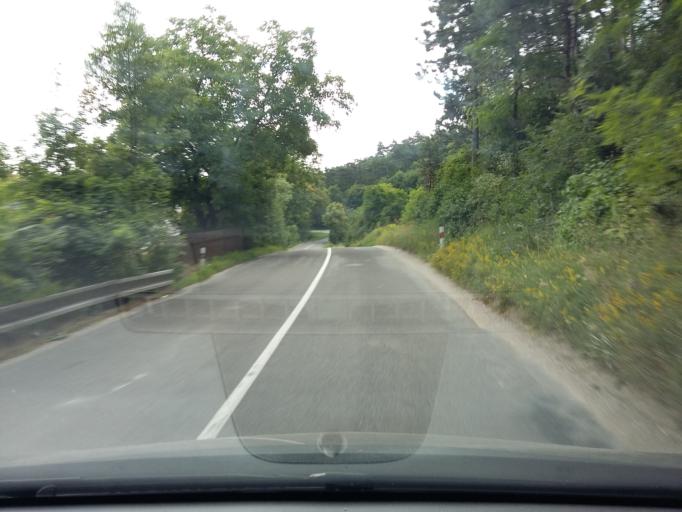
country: SK
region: Trnavsky
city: Smolenice
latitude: 48.5391
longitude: 17.4380
